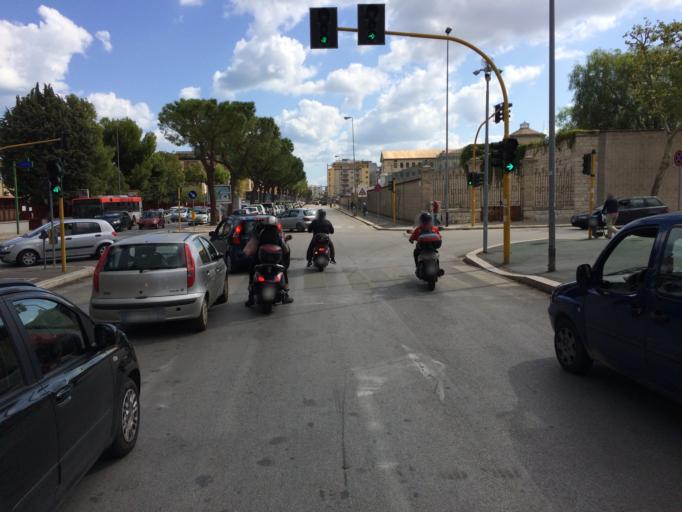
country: IT
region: Apulia
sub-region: Provincia di Bari
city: Bari
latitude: 41.1071
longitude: 16.8676
